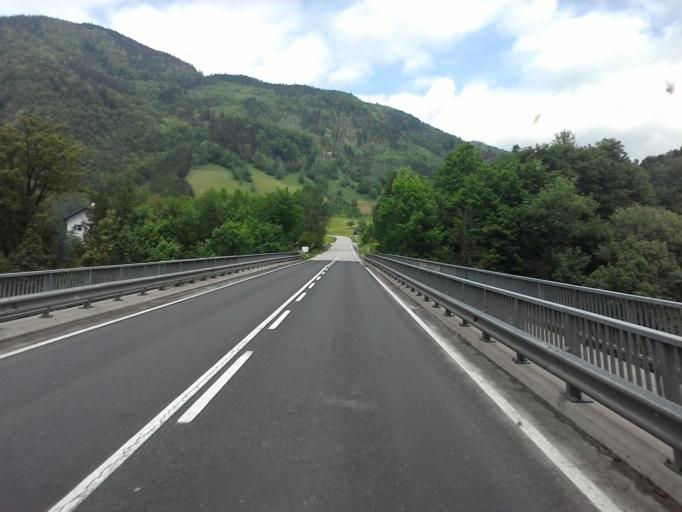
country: AT
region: Upper Austria
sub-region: Politischer Bezirk Steyr-Land
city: Weyer
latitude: 47.8524
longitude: 14.6410
